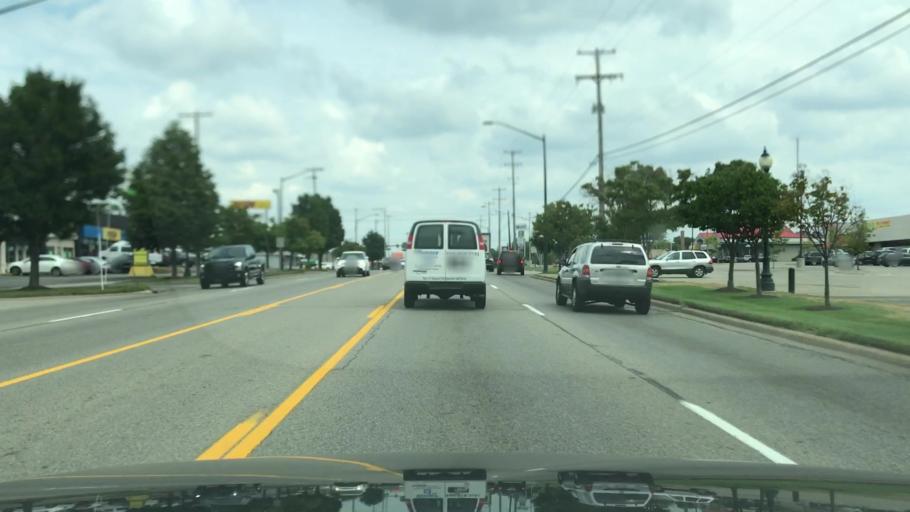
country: US
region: Michigan
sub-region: Kent County
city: Wyoming
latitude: 42.9133
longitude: -85.6884
